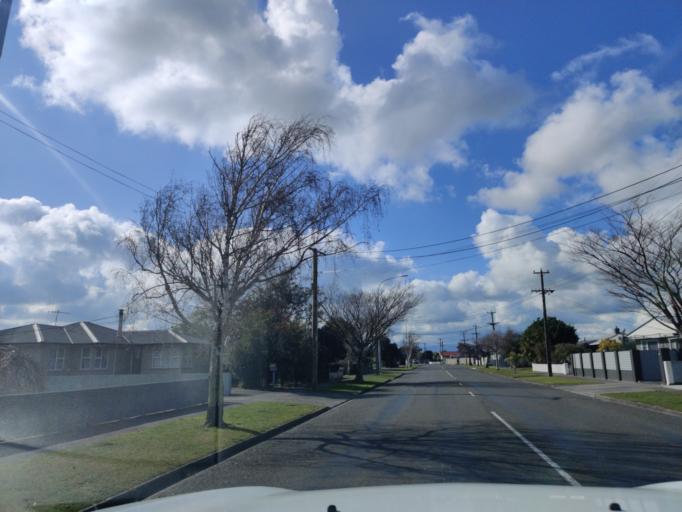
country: NZ
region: Manawatu-Wanganui
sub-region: Palmerston North City
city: Palmerston North
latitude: -40.3346
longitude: 175.6101
